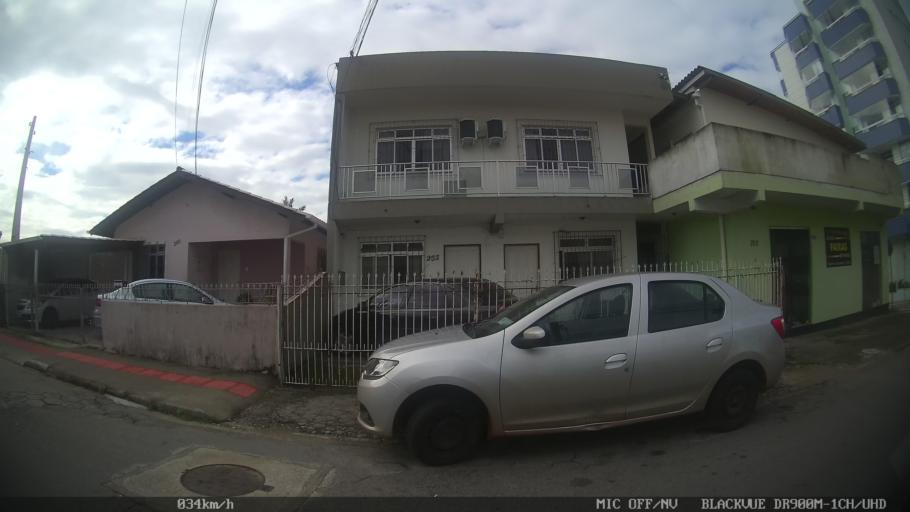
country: BR
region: Santa Catarina
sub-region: Sao Jose
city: Campinas
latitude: -27.5749
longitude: -48.6116
